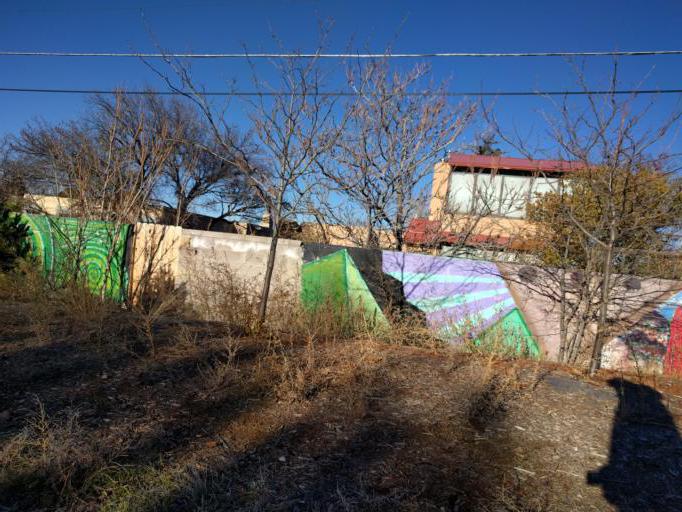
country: US
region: New Mexico
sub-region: Santa Fe County
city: Santa Fe
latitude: 35.6691
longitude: -105.9601
